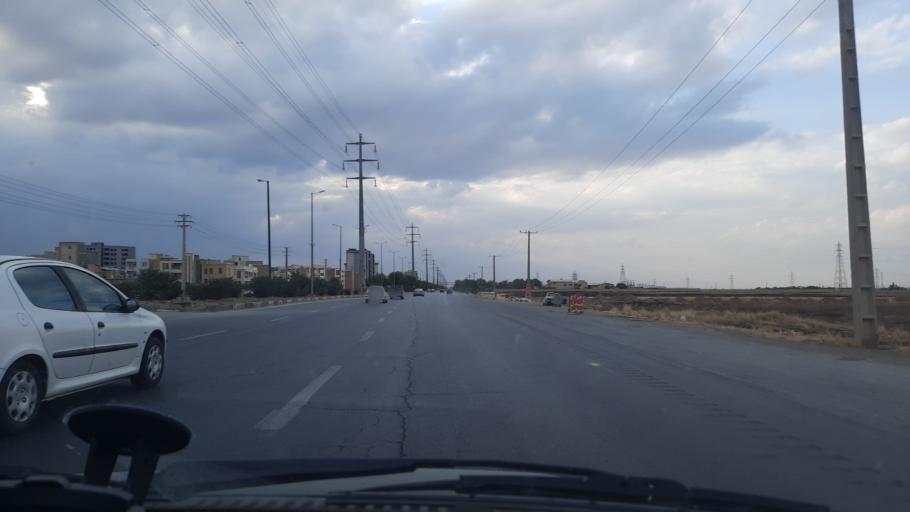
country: IR
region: Markazi
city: Arak
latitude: 34.1024
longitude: 49.7491
